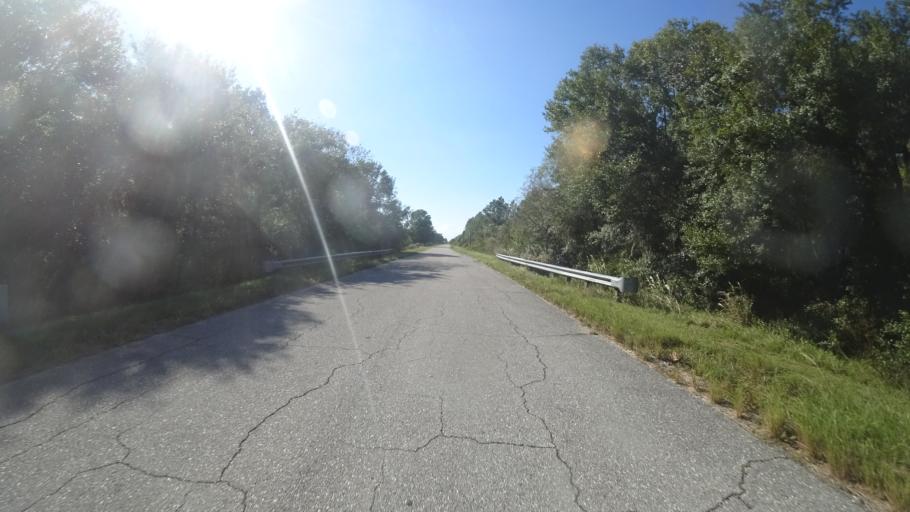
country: US
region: Florida
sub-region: Sarasota County
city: Fruitville
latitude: 27.4051
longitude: -82.2798
